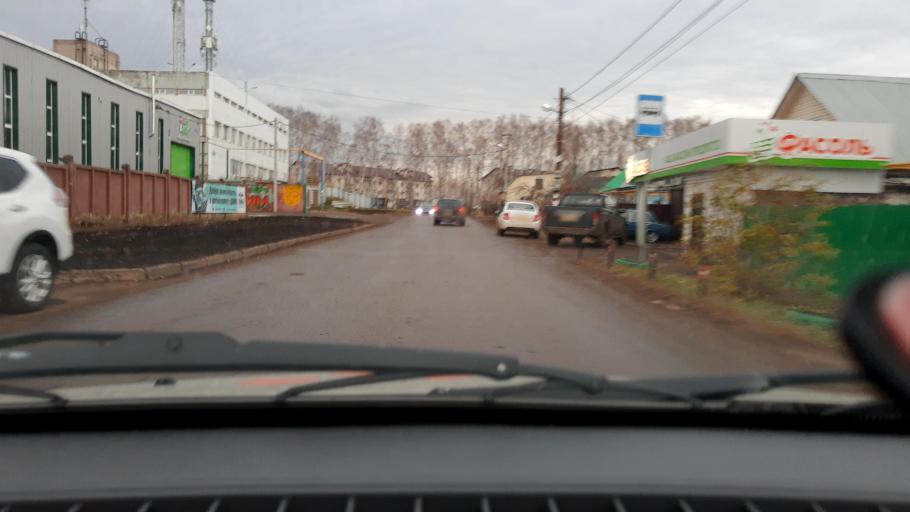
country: RU
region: Bashkortostan
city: Avdon
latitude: 54.6908
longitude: 55.7990
